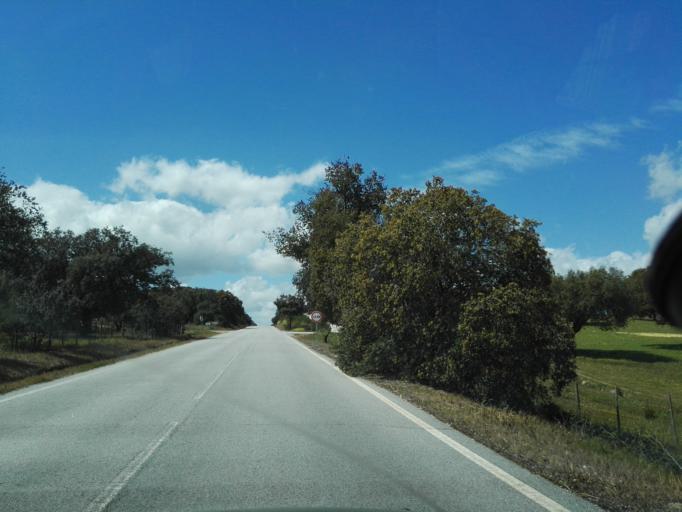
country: PT
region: Portalegre
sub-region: Campo Maior
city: Campo Maior
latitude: 38.9937
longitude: -7.1593
